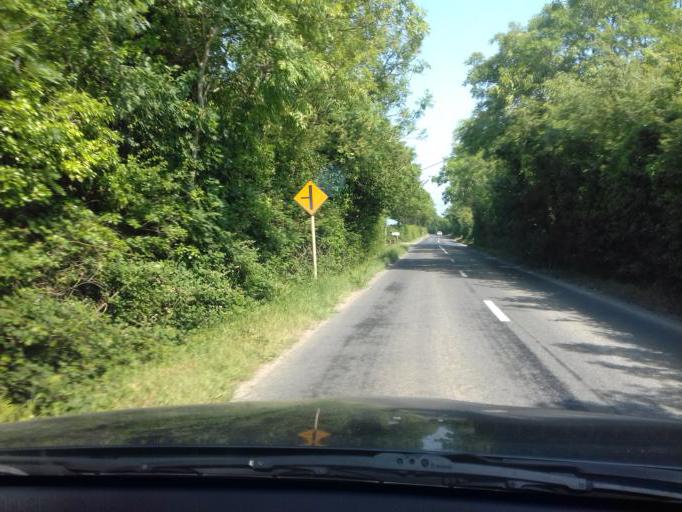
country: IE
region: Leinster
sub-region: An Mhi
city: Stamullin
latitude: 53.5982
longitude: -6.2494
